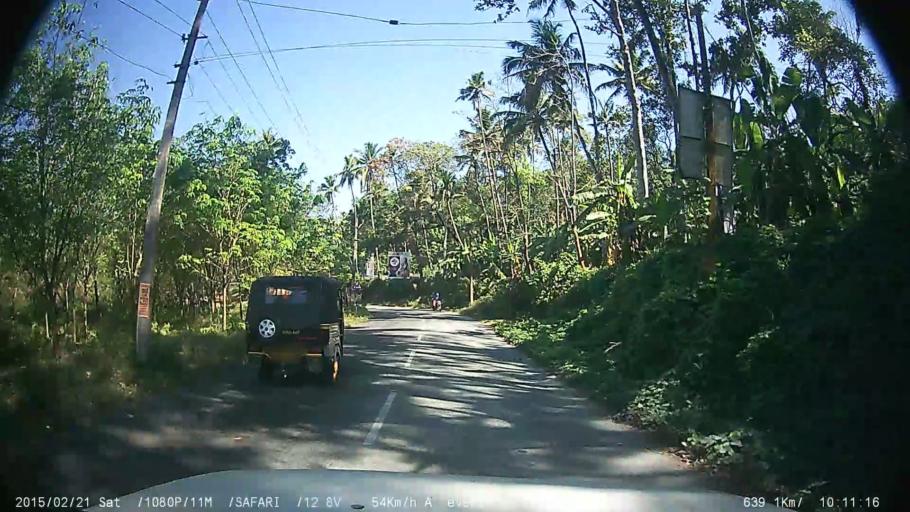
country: IN
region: Kerala
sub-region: Ernakulam
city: Muvattupuzha
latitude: 9.8833
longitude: 76.6199
